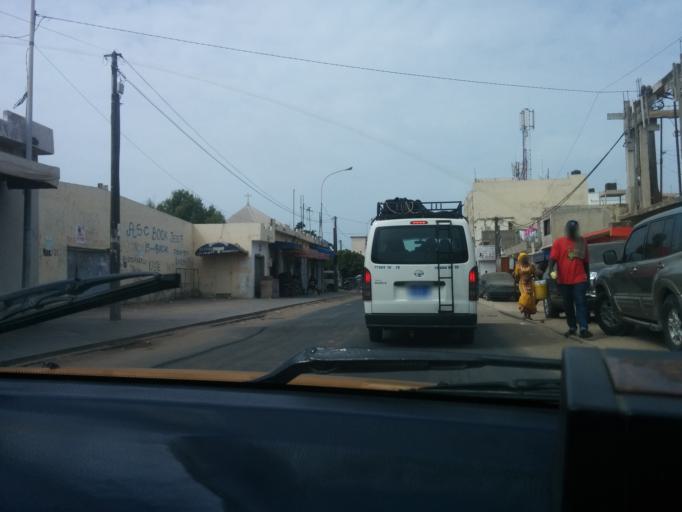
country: SN
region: Dakar
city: Pikine
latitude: 14.7581
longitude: -17.4362
